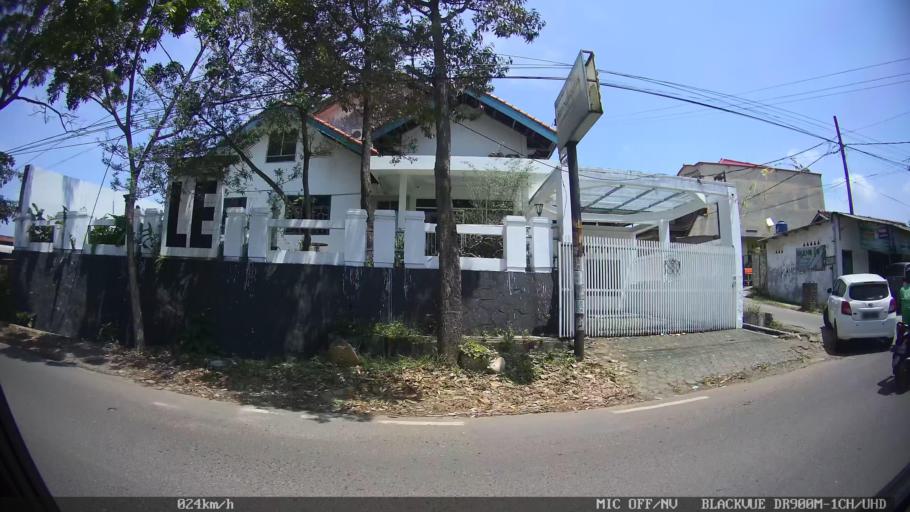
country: ID
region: Lampung
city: Kedaton
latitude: -5.3903
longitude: 105.2734
